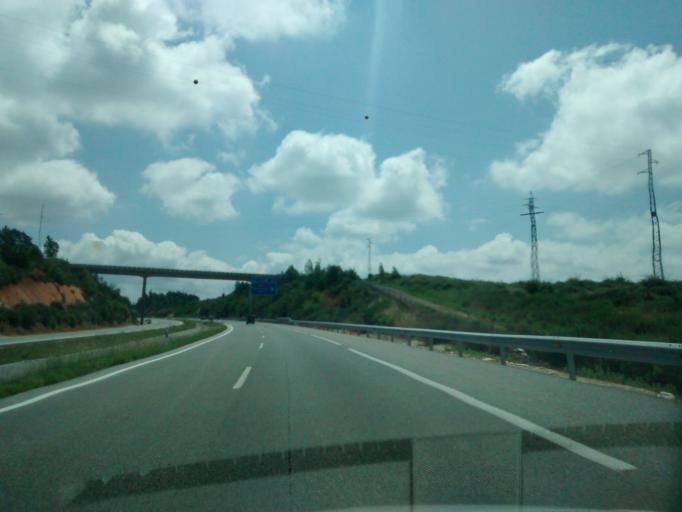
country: ES
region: Castille and Leon
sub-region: Provincia de Leon
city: Ponferrada
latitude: 42.5624
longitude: -6.5694
